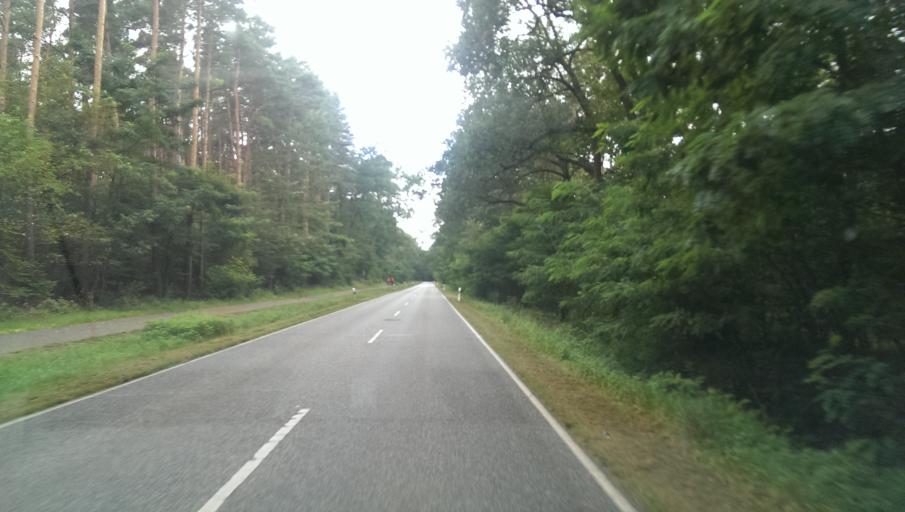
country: DE
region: Brandenburg
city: Leegebruch
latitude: 52.7223
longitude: 13.1710
